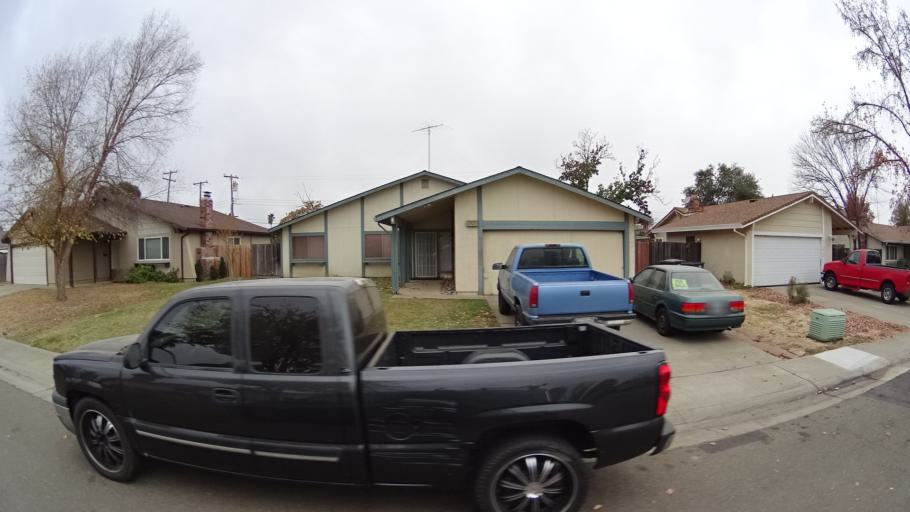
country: US
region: California
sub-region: Sacramento County
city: Citrus Heights
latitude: 38.6929
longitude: -121.3040
